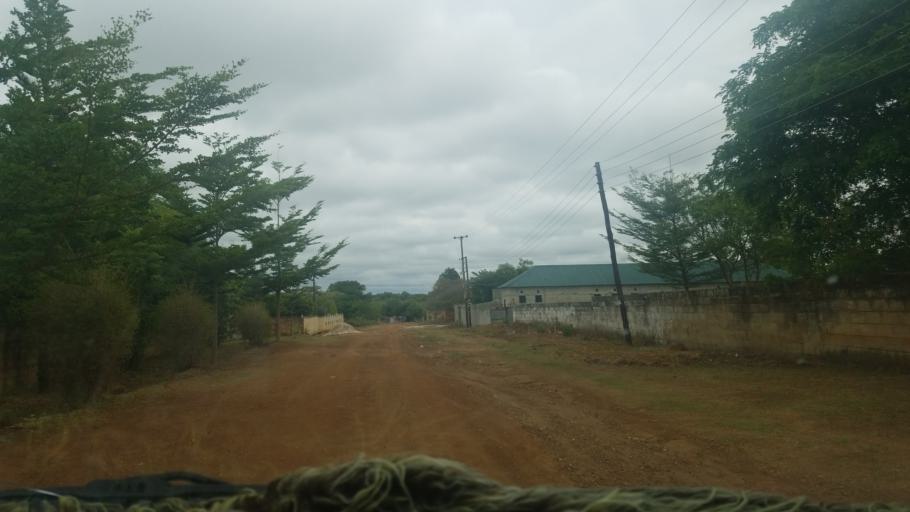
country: ZM
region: Luapula
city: Mansa
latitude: -11.1946
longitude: 28.9020
